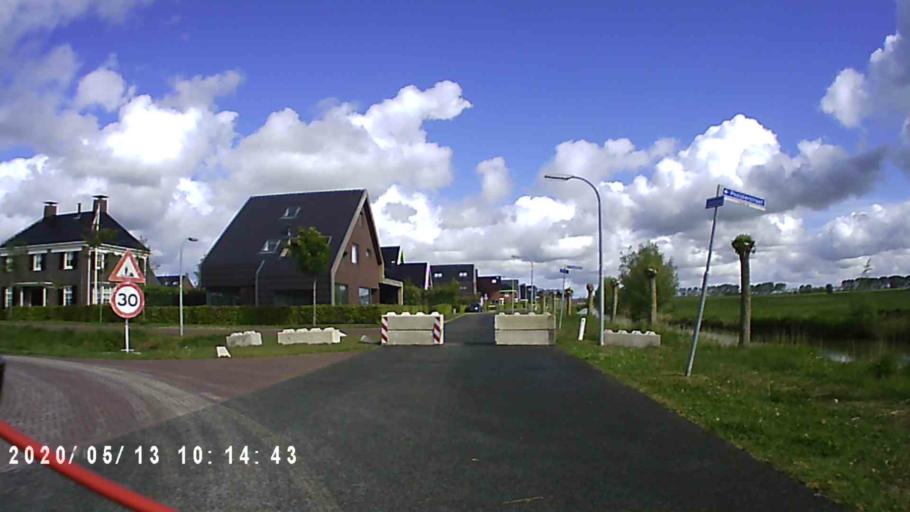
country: NL
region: Groningen
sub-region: Gemeente Zuidhorn
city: Zuidhorn
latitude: 53.2475
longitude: 6.4166
